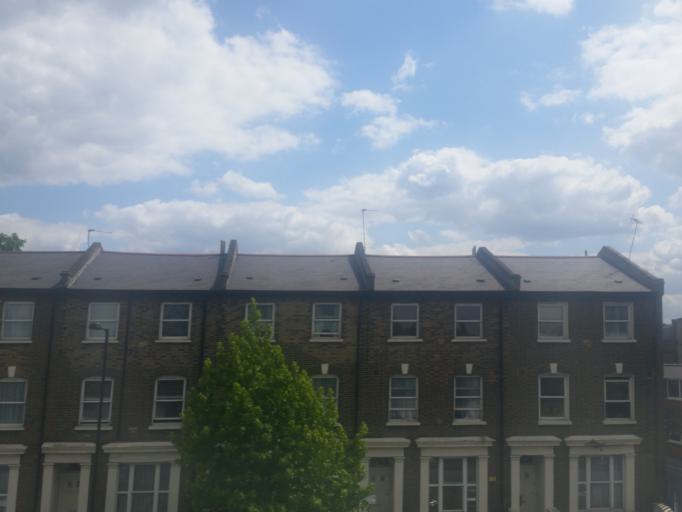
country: GB
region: England
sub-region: Greater London
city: Camberwell
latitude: 51.4744
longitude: -0.0969
